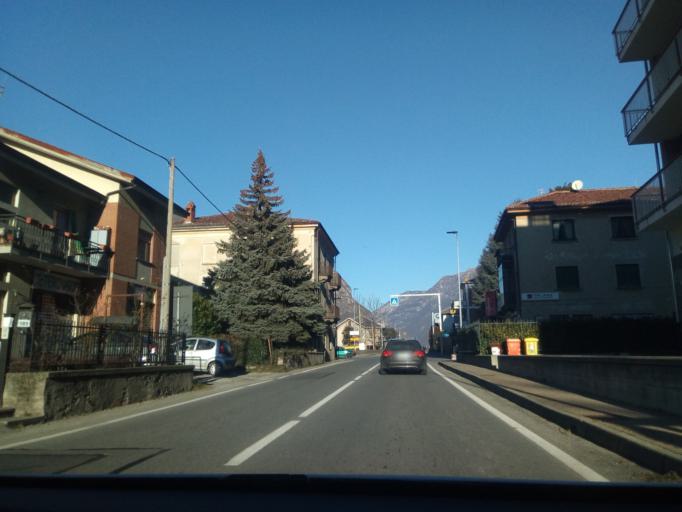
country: IT
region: Piedmont
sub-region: Provincia di Torino
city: Settimo Vittone
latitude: 45.5485
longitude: 7.8299
